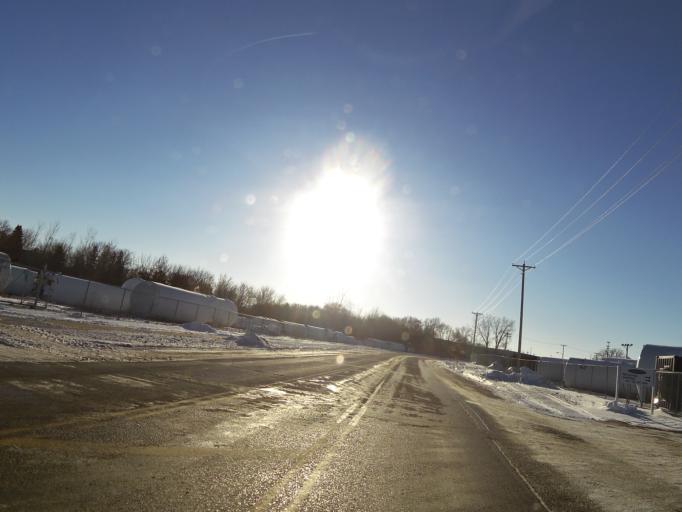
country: US
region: Minnesota
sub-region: Le Sueur County
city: New Prague
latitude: 44.5509
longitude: -93.5806
